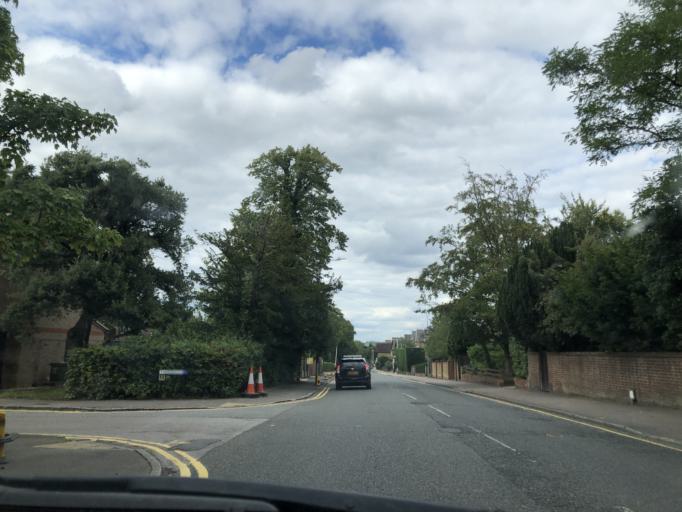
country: GB
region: England
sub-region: Kent
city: Sevenoaks
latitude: 51.2789
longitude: 0.1941
